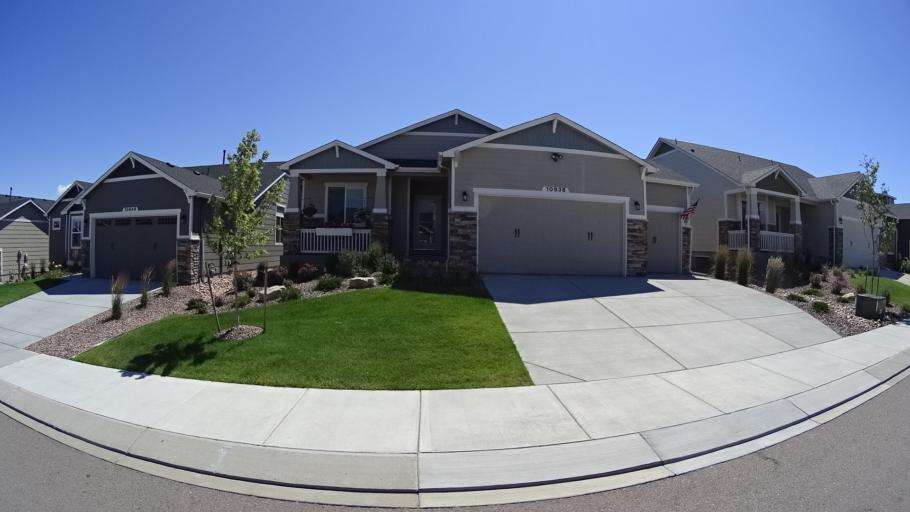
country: US
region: Colorado
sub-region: El Paso County
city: Black Forest
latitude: 38.9906
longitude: -104.7613
